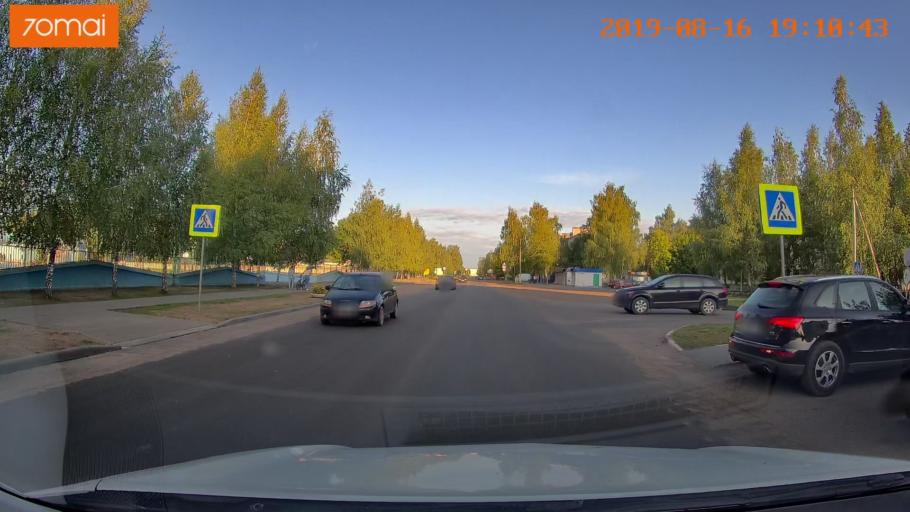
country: BY
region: Mogilev
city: Asipovichy
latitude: 53.3231
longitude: 28.6432
